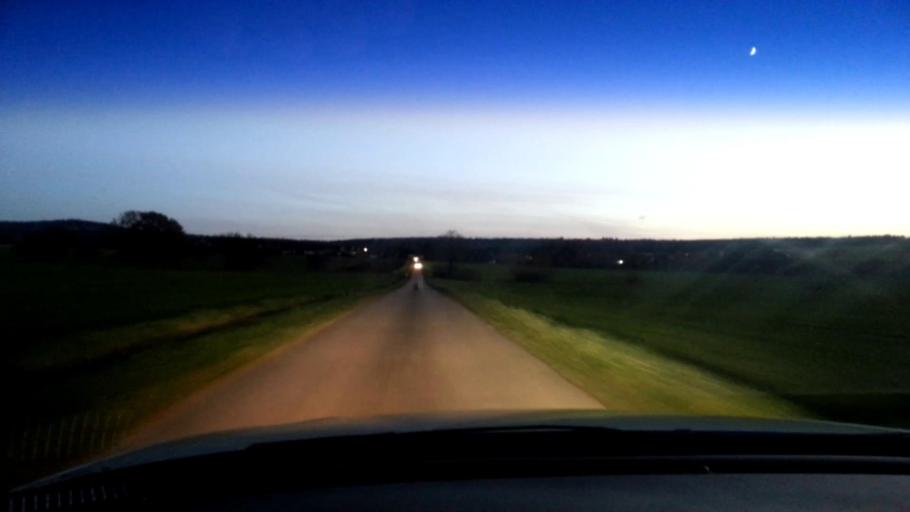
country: DE
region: Bavaria
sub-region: Upper Franconia
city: Litzendorf
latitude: 49.9464
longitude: 10.9961
